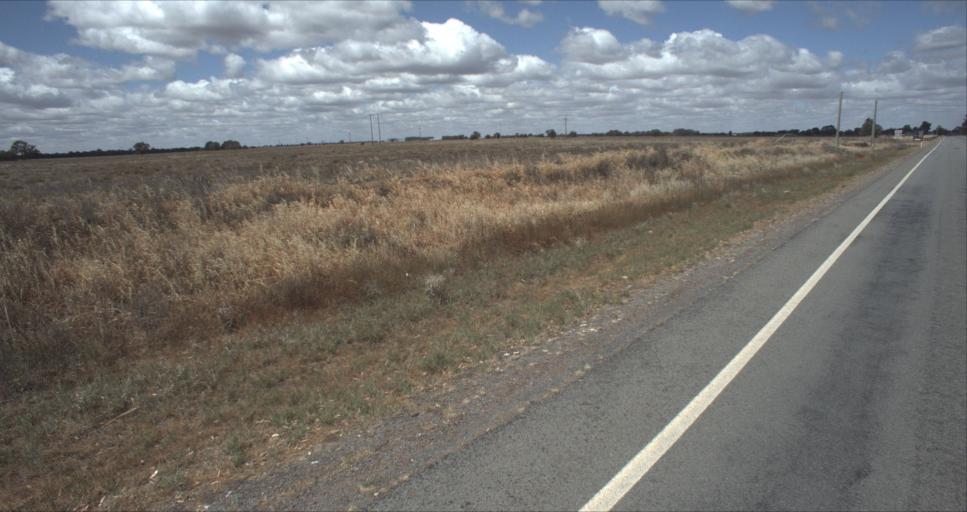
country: AU
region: New South Wales
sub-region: Murrumbidgee Shire
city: Darlington Point
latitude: -34.5091
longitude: 146.1866
